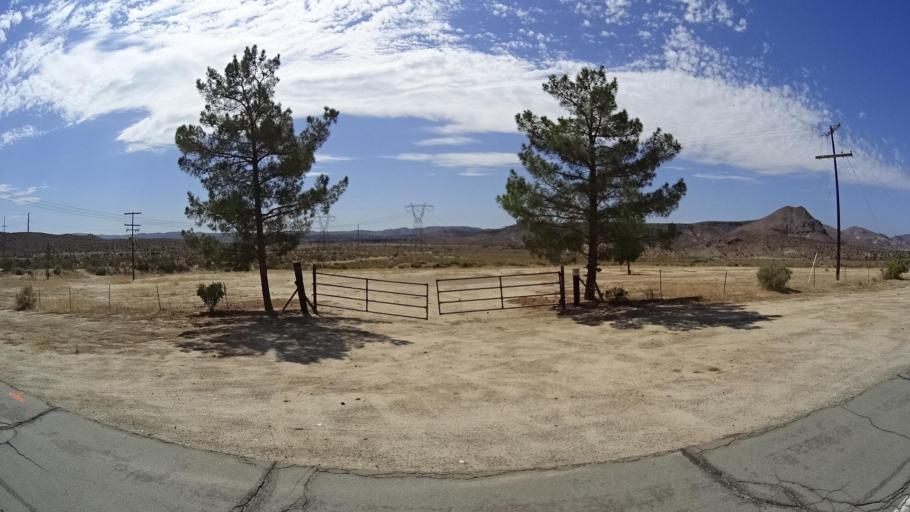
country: MX
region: Baja California
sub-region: Tecate
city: Cereso del Hongo
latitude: 32.6331
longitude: -116.1642
